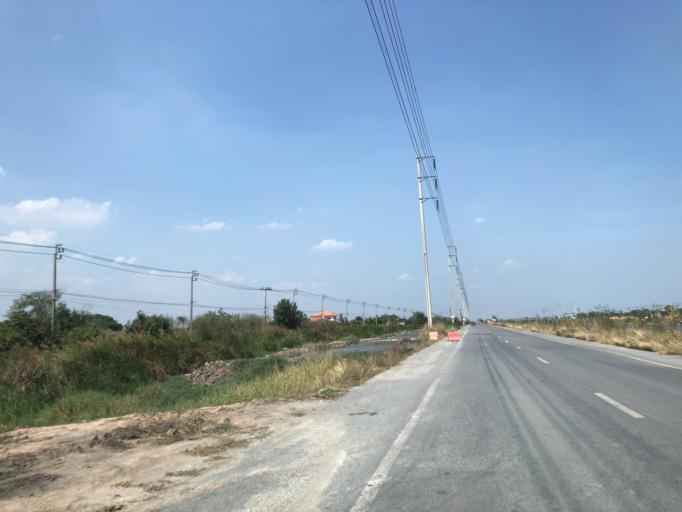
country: TH
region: Samut Prakan
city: Bang Bo District
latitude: 13.5214
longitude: 100.7470
